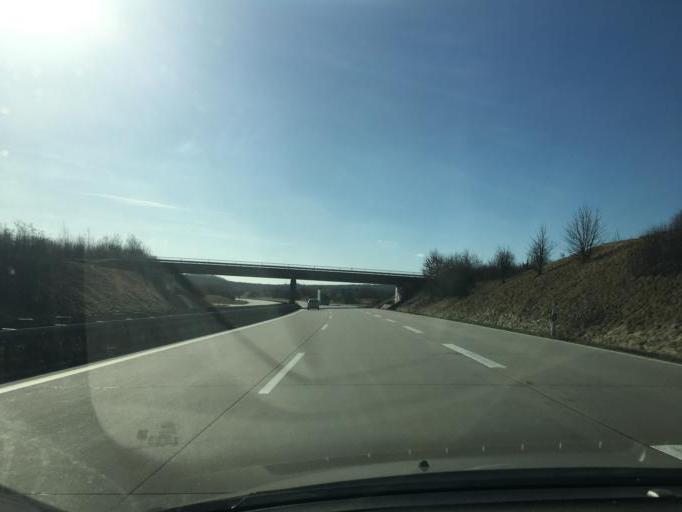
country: DE
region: Saxony
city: Muhlau
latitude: 50.8908
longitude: 12.7467
